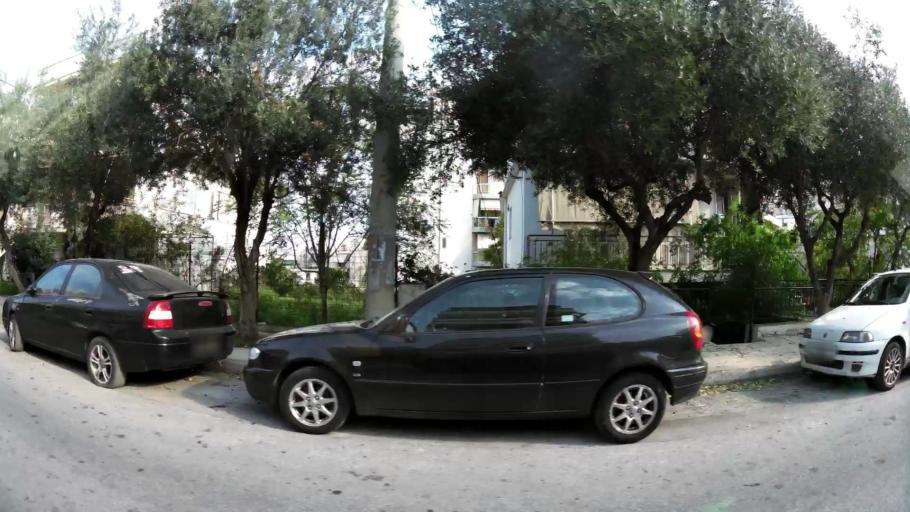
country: GR
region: Attica
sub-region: Nomarchia Athinas
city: Galatsi
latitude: 38.0098
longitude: 23.7446
